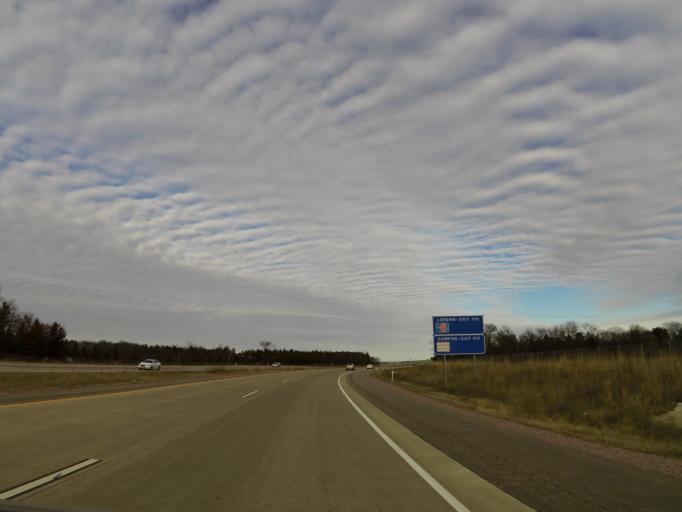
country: US
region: Wisconsin
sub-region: Sauk County
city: Lake Delton
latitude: 43.5531
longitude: -89.7865
